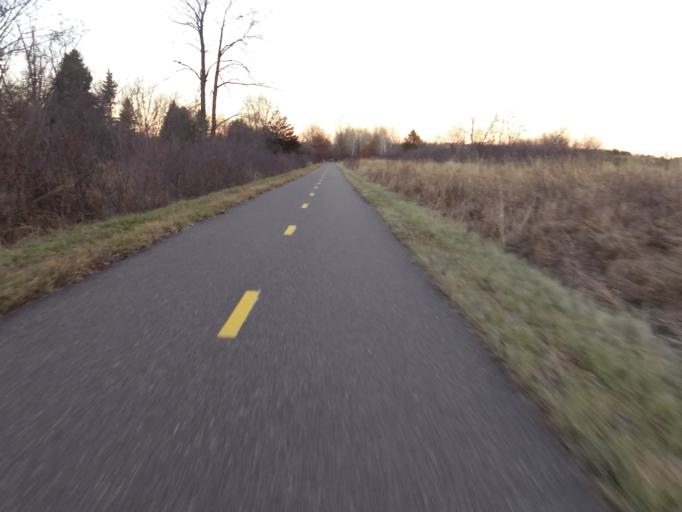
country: US
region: Minnesota
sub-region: Washington County
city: Grant
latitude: 45.0941
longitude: -92.8776
